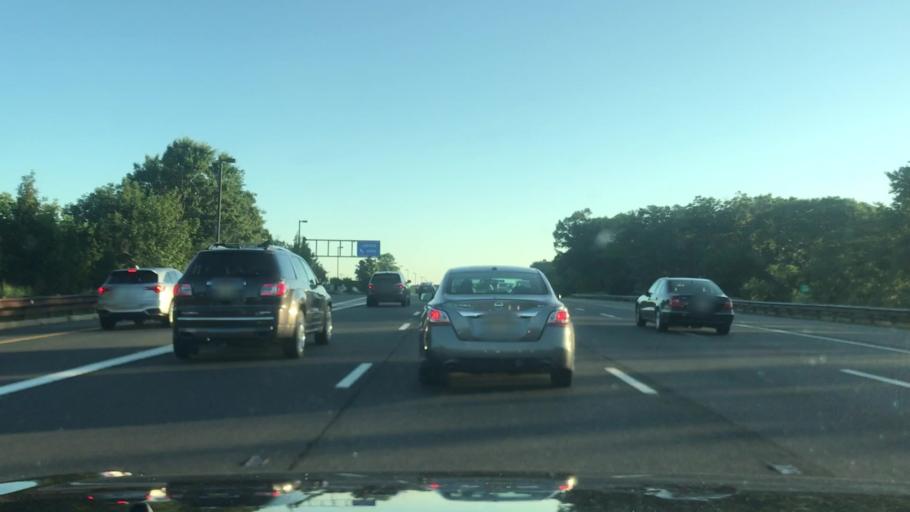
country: US
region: New Jersey
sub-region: Monmouth County
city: Shark River Hills
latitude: 40.1946
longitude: -74.0991
